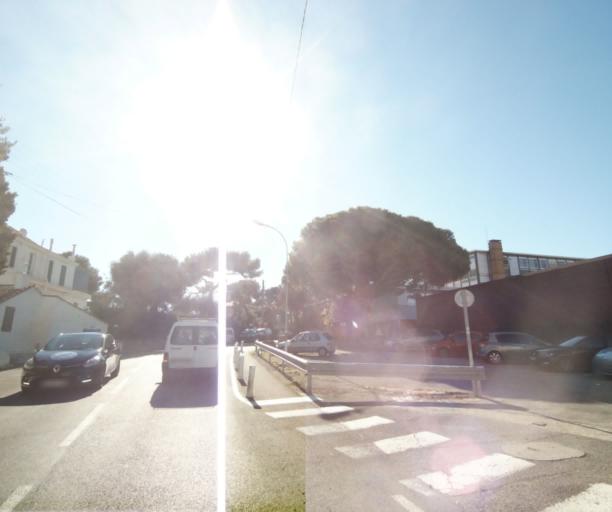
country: FR
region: Provence-Alpes-Cote d'Azur
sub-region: Departement des Alpes-Maritimes
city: Antibes
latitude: 43.5743
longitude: 7.1196
